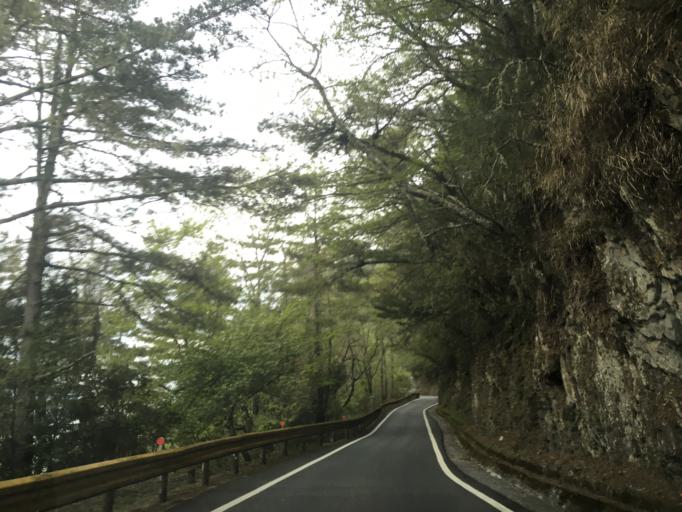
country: TW
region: Taiwan
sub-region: Hualien
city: Hualian
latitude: 24.1727
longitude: 121.3794
